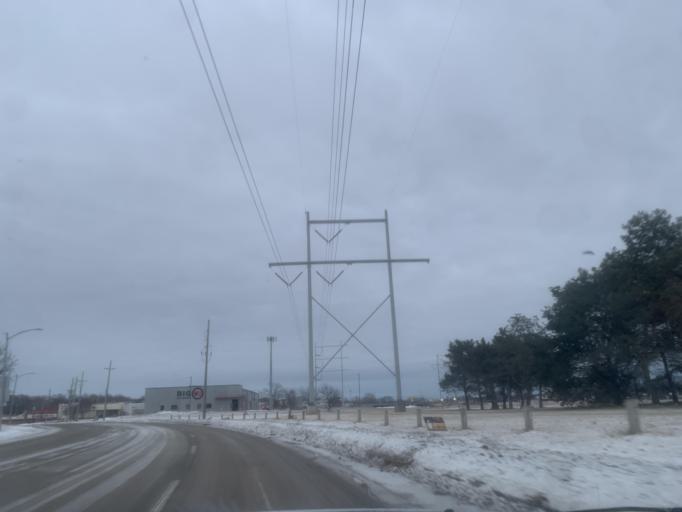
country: US
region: Nebraska
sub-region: Douglas County
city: Ralston
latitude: 41.2297
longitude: -96.0472
